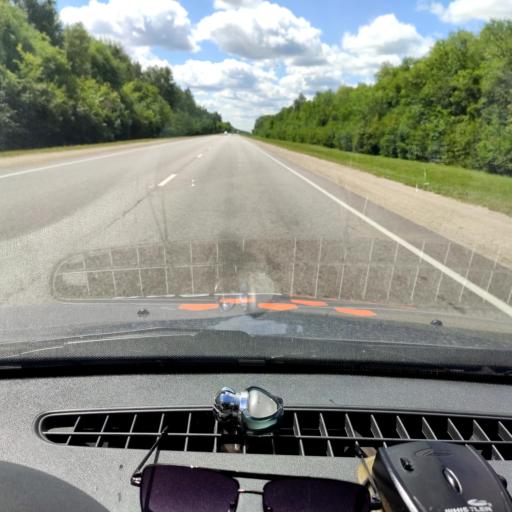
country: RU
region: Lipetsk
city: Borinskoye
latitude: 52.3988
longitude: 39.2360
